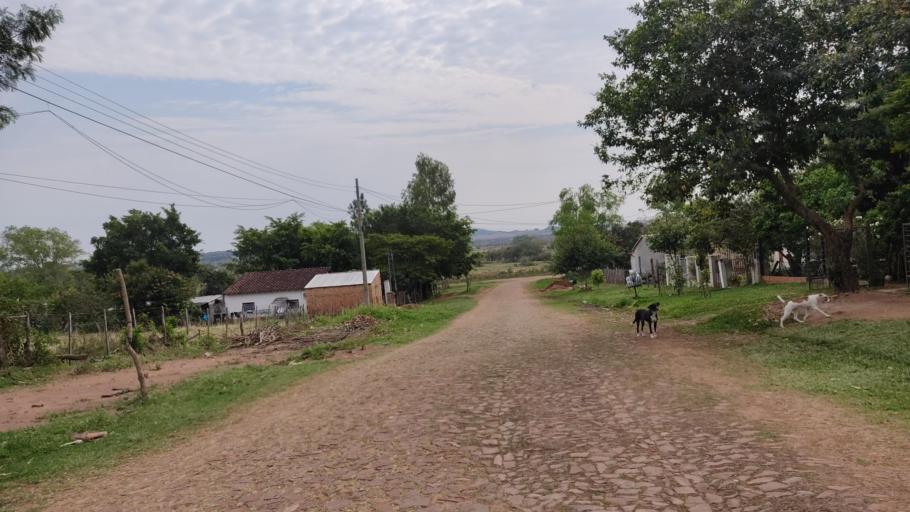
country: PY
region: Misiones
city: San Juan Bautista
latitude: -26.6601
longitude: -57.1505
